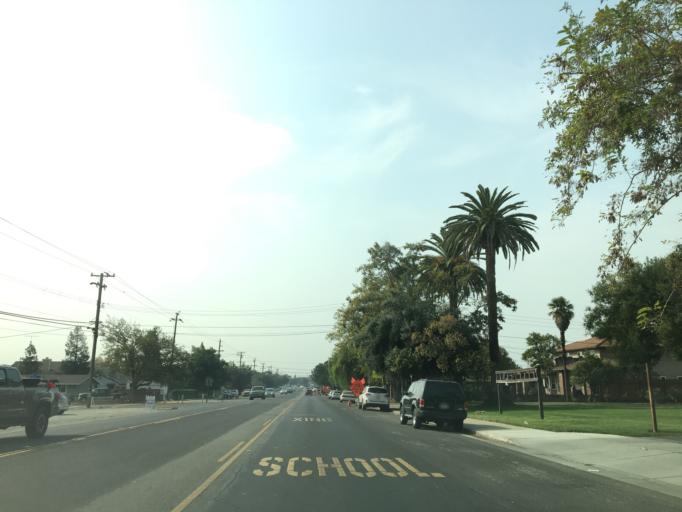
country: US
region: California
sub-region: Santa Clara County
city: Alum Rock
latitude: 37.3713
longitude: -121.8241
